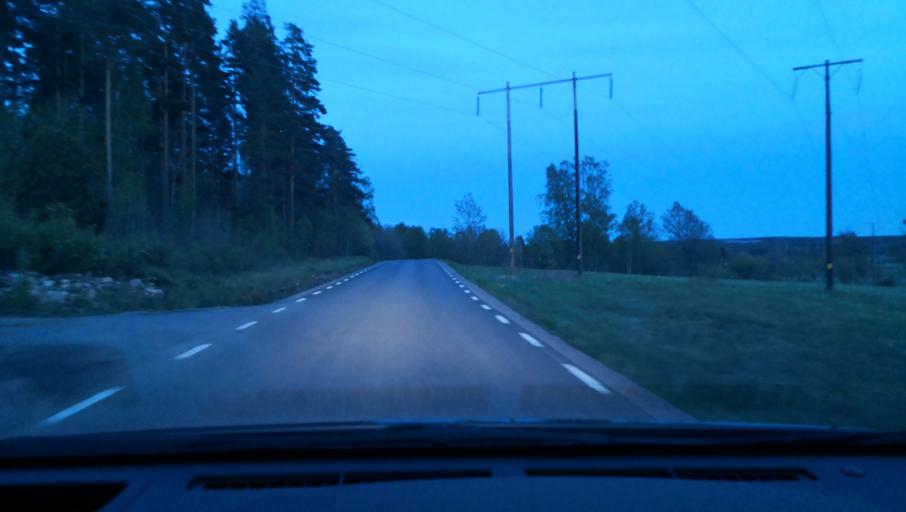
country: SE
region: OErebro
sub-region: Askersunds Kommun
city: Asbro
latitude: 59.0683
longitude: 14.9848
